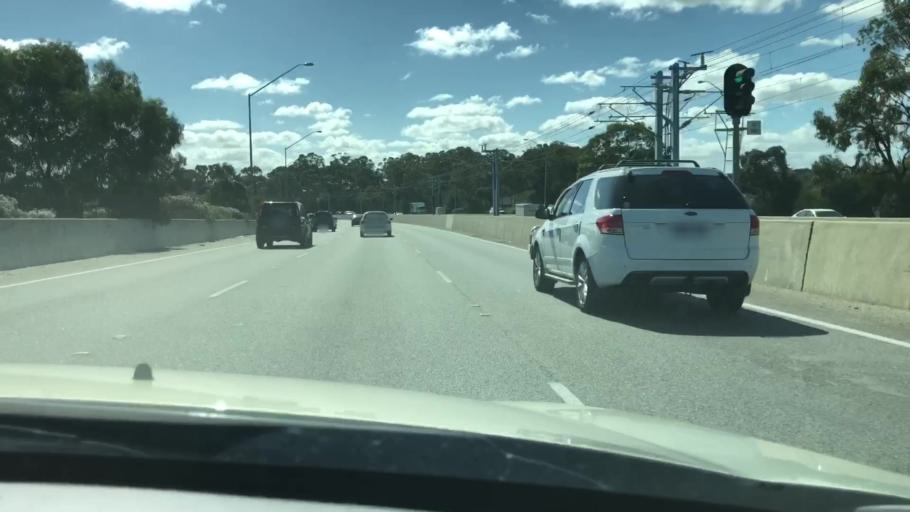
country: AU
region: Western Australia
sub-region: Canning
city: Rossmoyne
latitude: -32.0310
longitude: 115.8598
